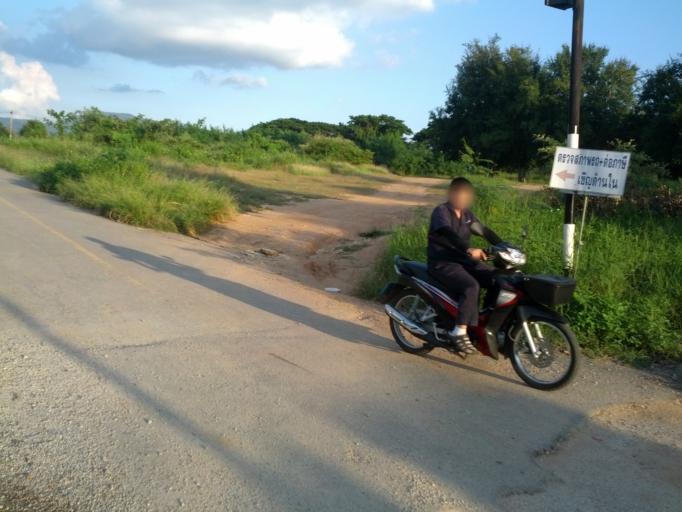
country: TH
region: Lampang
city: Lampang
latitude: 18.2888
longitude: 99.5114
